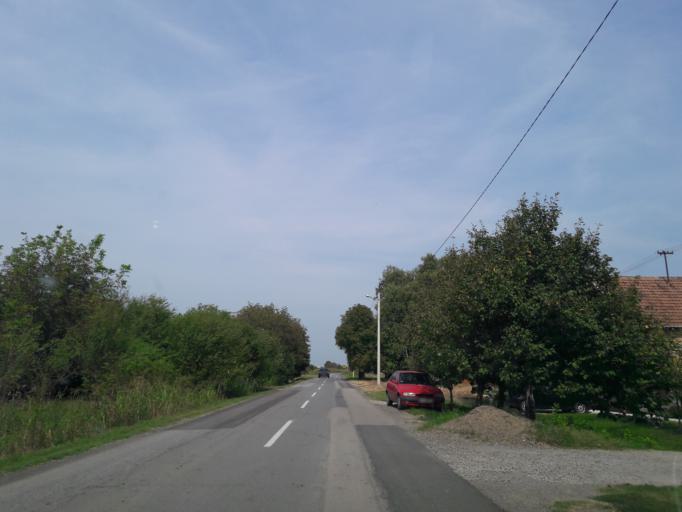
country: HR
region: Vukovarsko-Srijemska
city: Bobota
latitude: 45.4292
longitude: 18.8607
